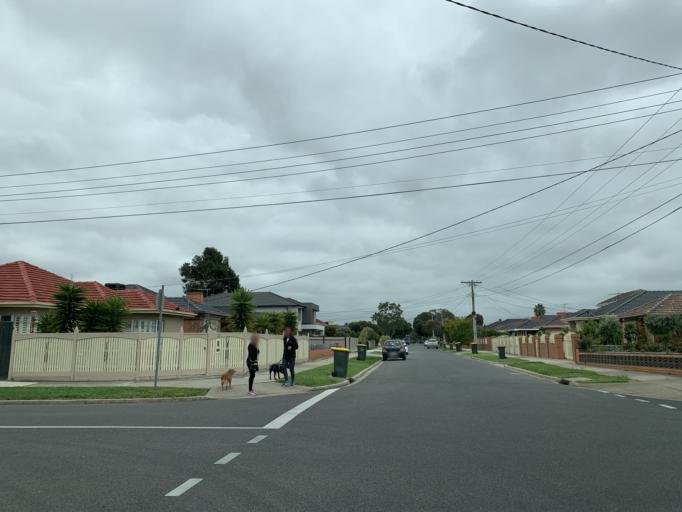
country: AU
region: Victoria
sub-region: Moonee Valley
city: Essendon West
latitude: -37.7574
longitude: 144.8588
